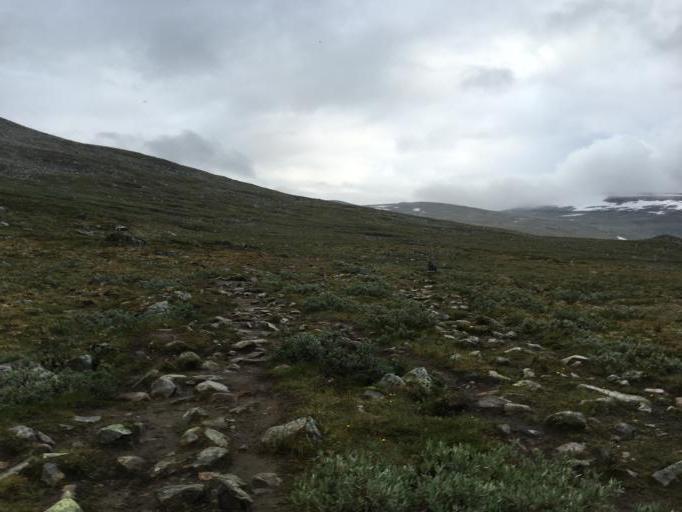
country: NO
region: Oppland
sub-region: Lom
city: Fossbergom
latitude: 61.6163
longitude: 8.6468
